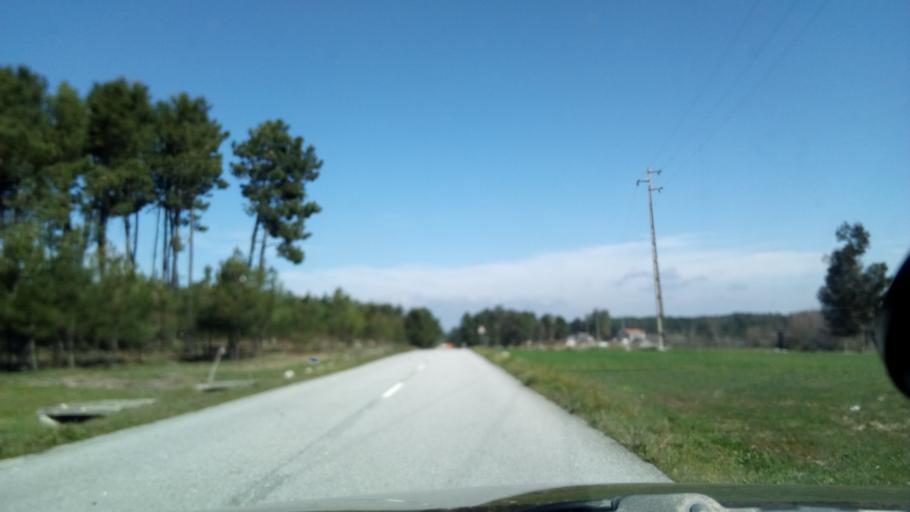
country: PT
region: Guarda
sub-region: Fornos de Algodres
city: Fornos de Algodres
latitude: 40.6412
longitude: -7.5315
